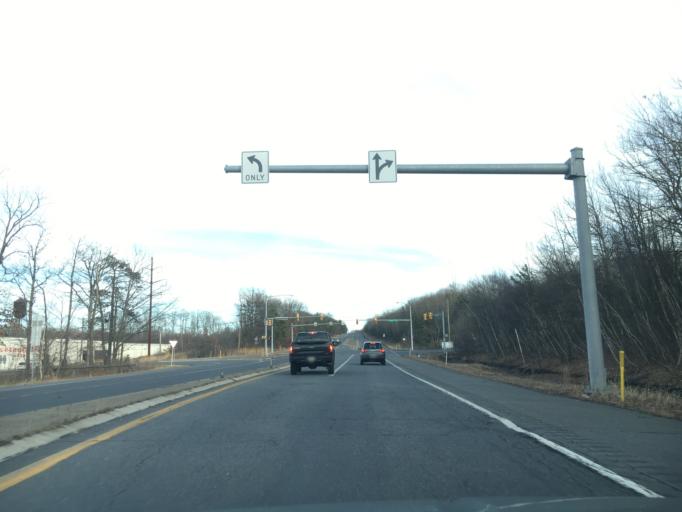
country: US
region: Pennsylvania
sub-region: Luzerne County
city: Hazleton
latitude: 40.9344
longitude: -75.9735
